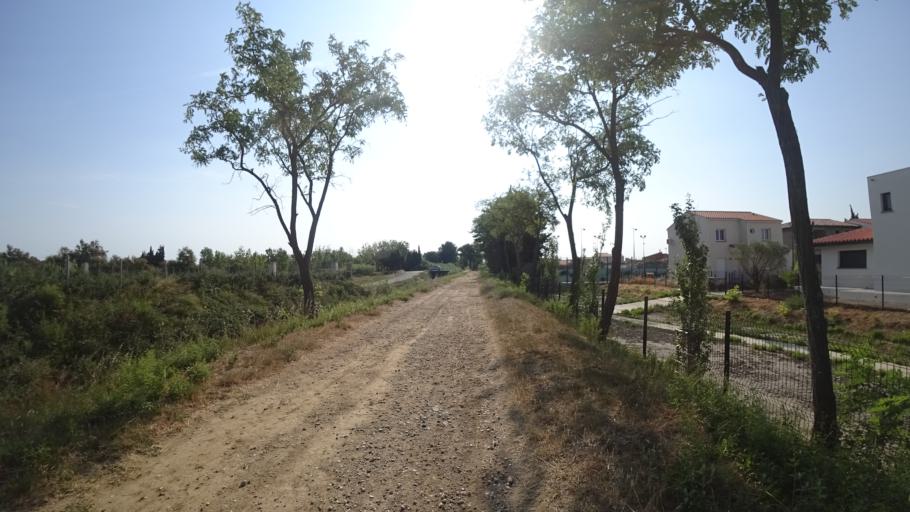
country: FR
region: Languedoc-Roussillon
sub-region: Departement des Pyrenees-Orientales
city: Saint-Laurent-de-la-Salanque
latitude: 42.7806
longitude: 2.9891
